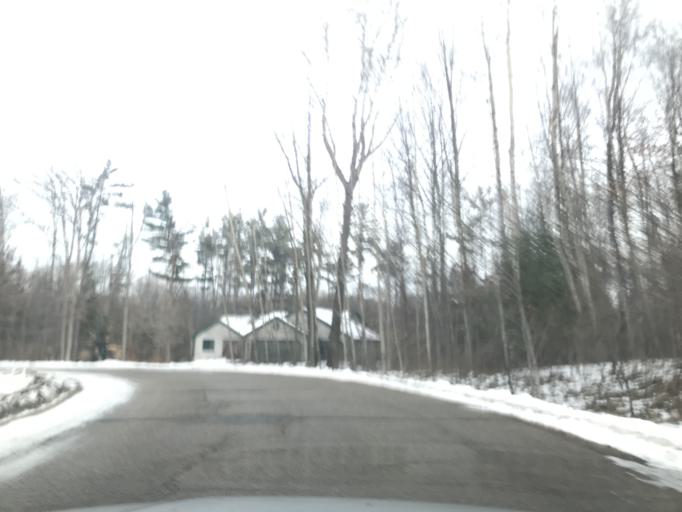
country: US
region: Wisconsin
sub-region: Brown County
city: Suamico
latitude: 44.6904
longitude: -88.0529
